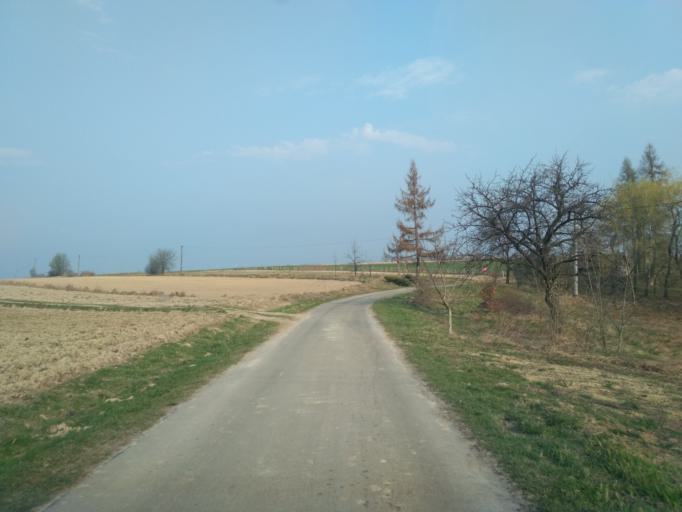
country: PL
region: Subcarpathian Voivodeship
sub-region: Powiat ropczycko-sedziszowski
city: Wielopole Skrzynskie
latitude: 49.9085
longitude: 21.5995
